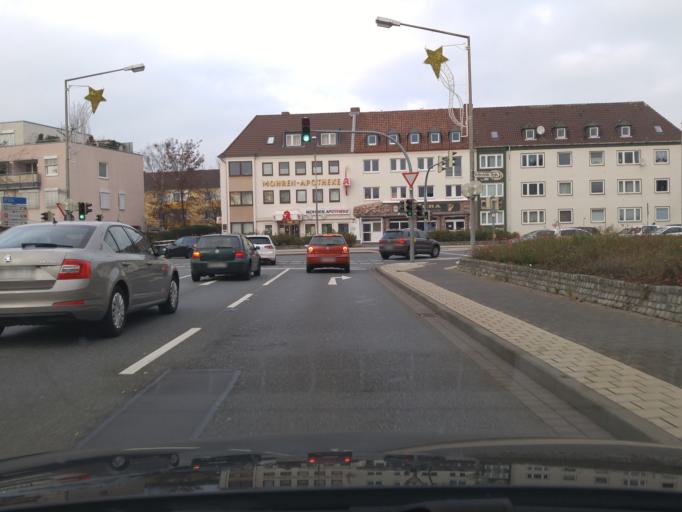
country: DE
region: Lower Saxony
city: Wolfsburg
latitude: 52.4238
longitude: 10.7927
